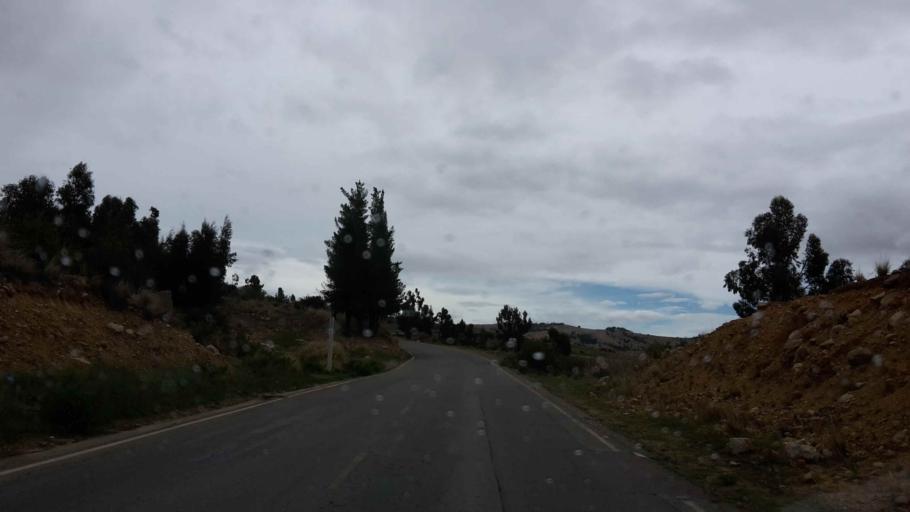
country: BO
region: Cochabamba
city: Arani
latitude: -17.4600
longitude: -65.6763
